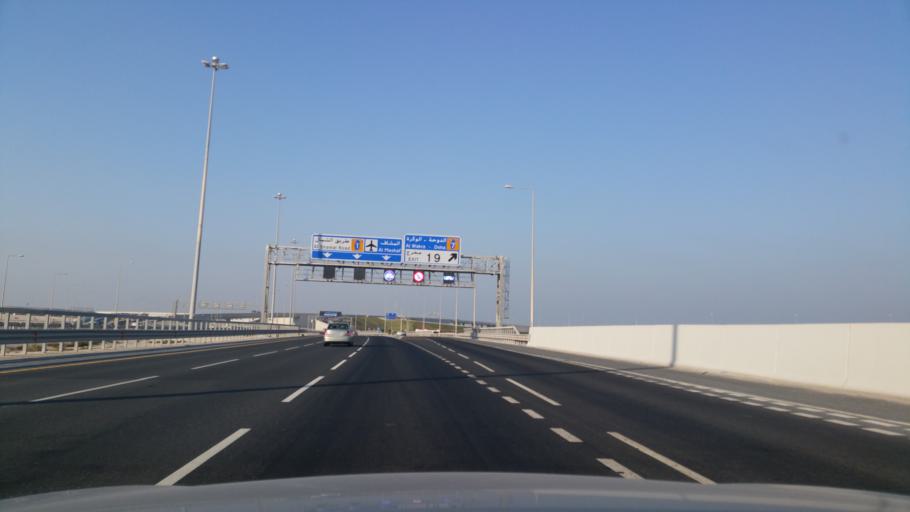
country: QA
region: Al Wakrah
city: Al Wakrah
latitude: 25.1165
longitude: 51.5866
